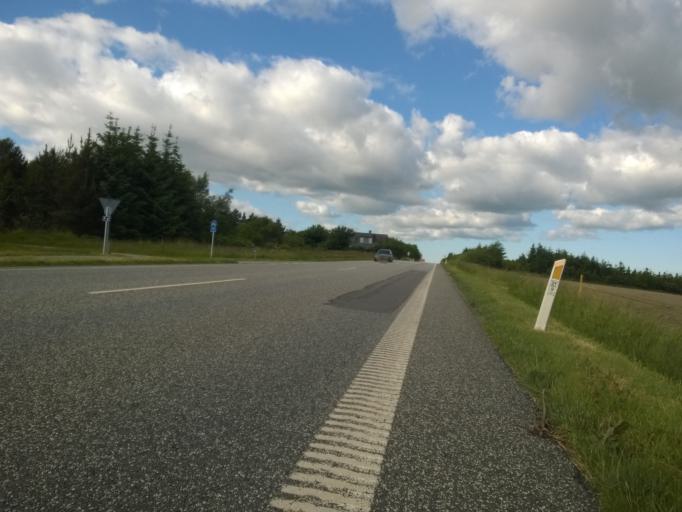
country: DK
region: Central Jutland
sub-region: Holstebro Kommune
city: Vinderup
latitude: 56.5146
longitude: 8.8081
